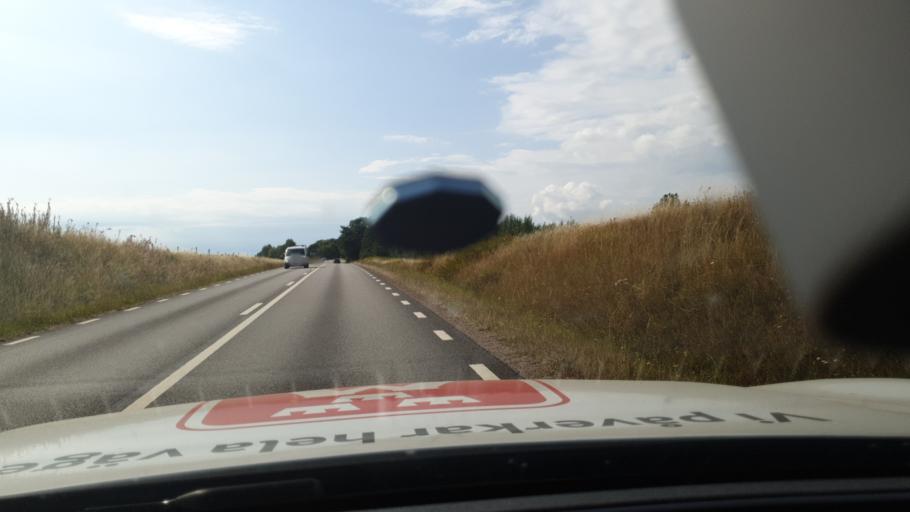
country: SE
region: Skane
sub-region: Svedala Kommun
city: Svedala
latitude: 55.4529
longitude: 13.2340
